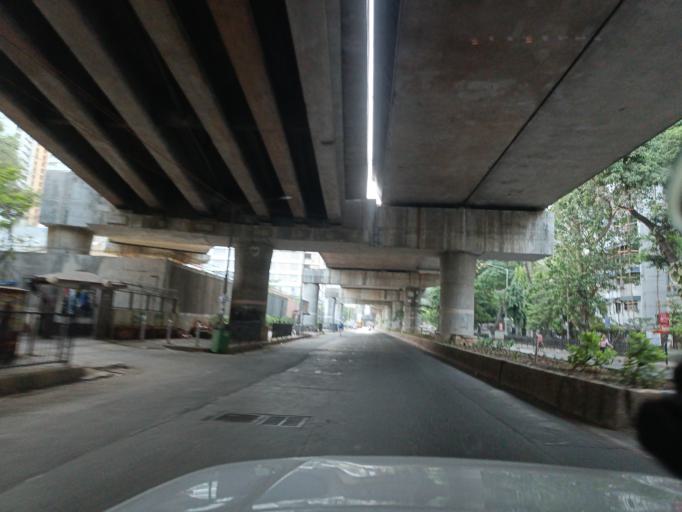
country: IN
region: Maharashtra
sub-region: Mumbai Suburban
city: Powai
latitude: 19.1293
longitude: 72.8260
